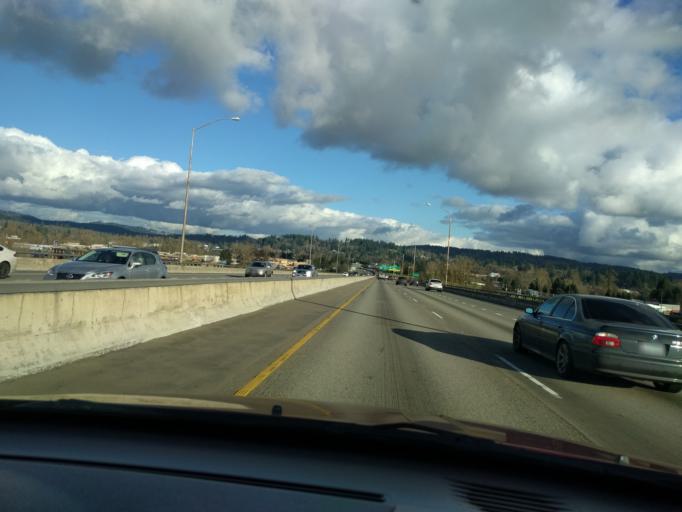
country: US
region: Oregon
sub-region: Clackamas County
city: Oregon City
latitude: 45.3640
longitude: -122.6056
